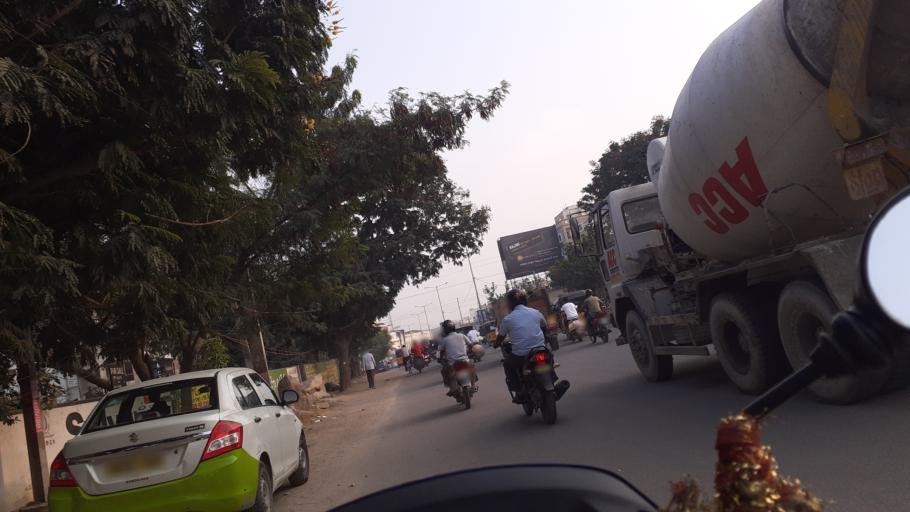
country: IN
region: Telangana
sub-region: Rangareddi
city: Kukatpalli
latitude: 17.4696
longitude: 78.3658
